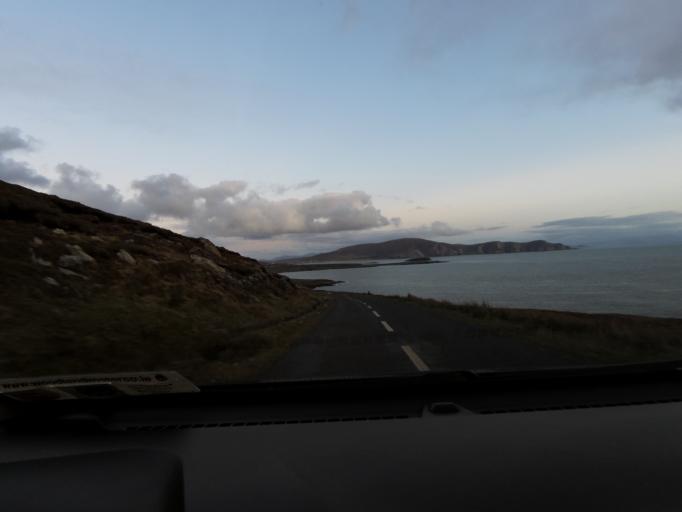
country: IE
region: Connaught
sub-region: Maigh Eo
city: Belmullet
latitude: 53.9693
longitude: -10.1580
